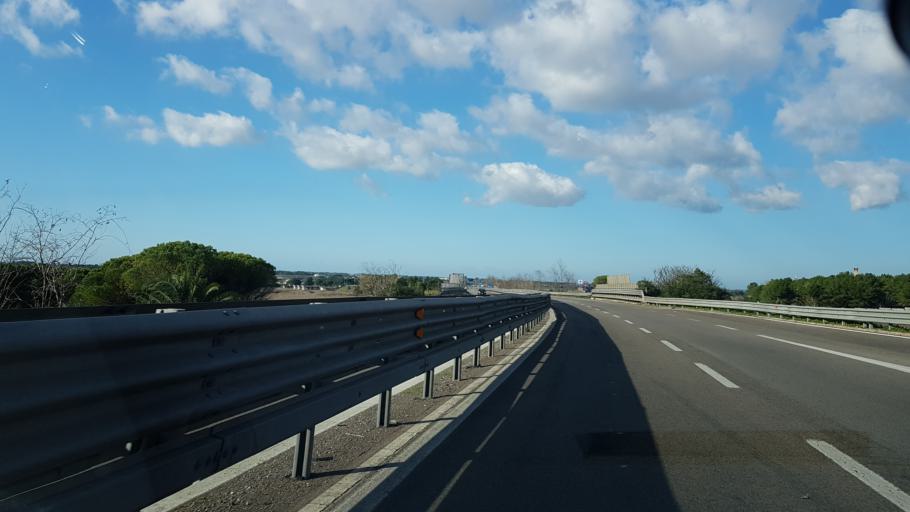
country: IT
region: Apulia
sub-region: Provincia di Lecce
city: Castromediano
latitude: 40.3260
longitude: 18.1624
